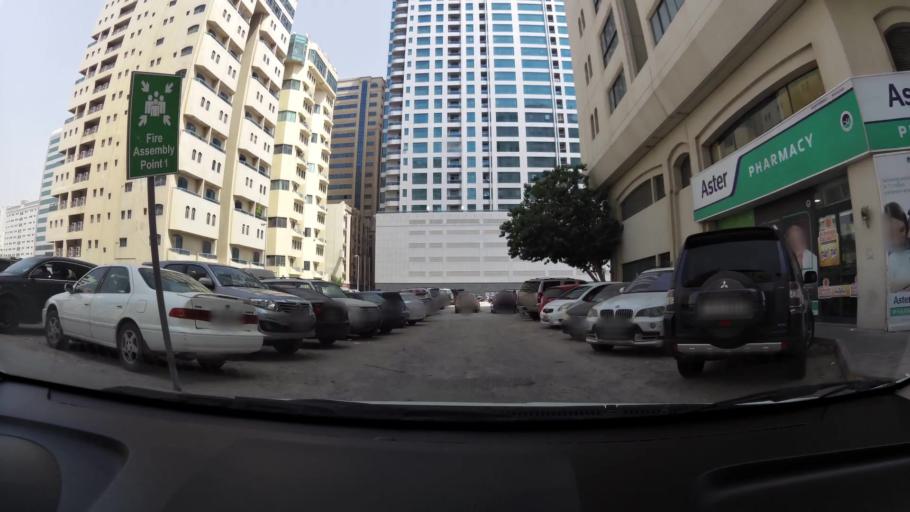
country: AE
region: Ash Shariqah
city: Sharjah
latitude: 25.3361
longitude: 55.3882
